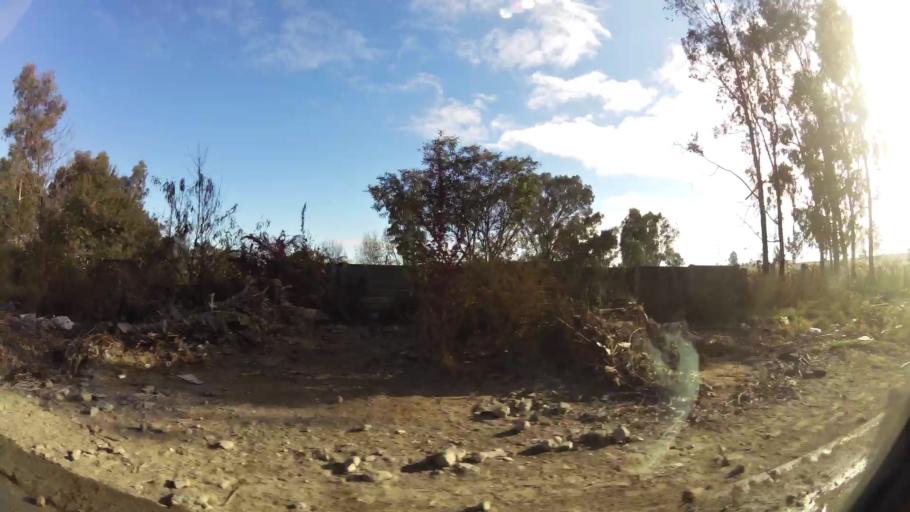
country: ZA
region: Gauteng
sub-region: City of Johannesburg Metropolitan Municipality
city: Modderfontein
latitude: -26.0399
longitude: 28.1673
